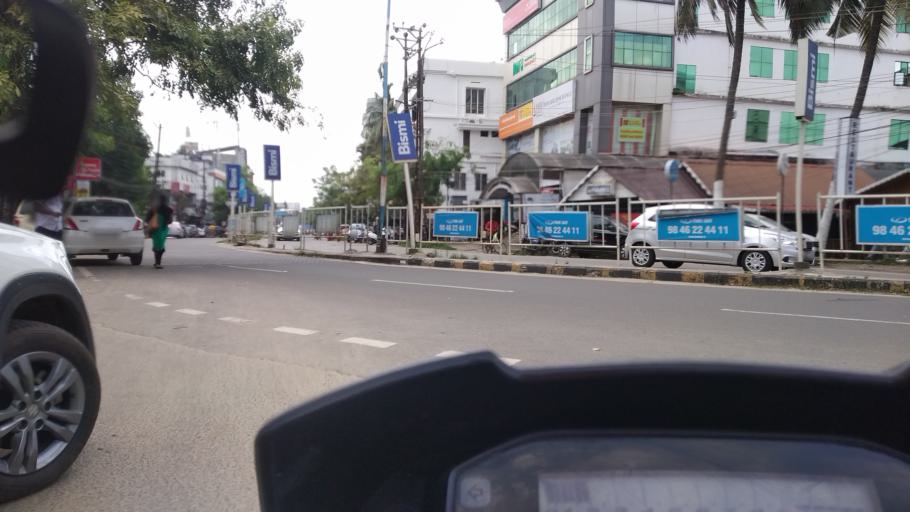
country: IN
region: Kerala
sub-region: Ernakulam
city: Cochin
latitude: 9.9906
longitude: 76.2935
